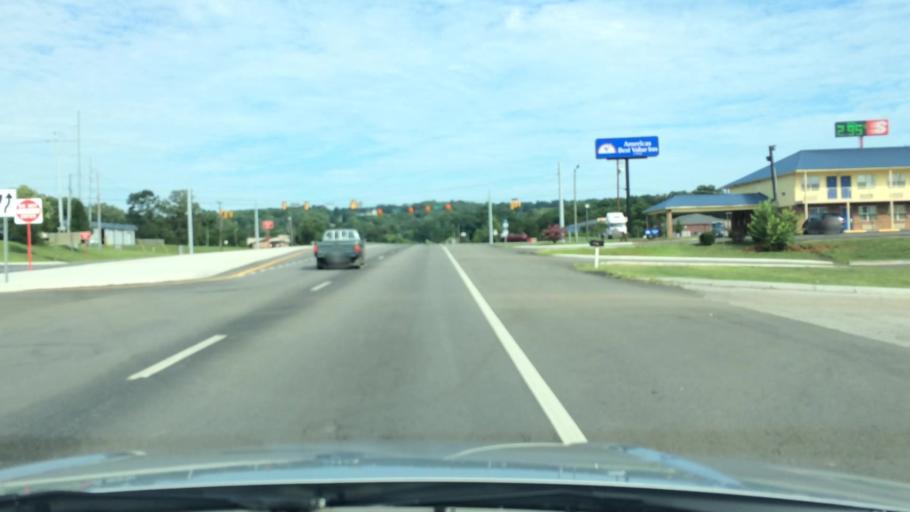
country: US
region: Tennessee
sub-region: McMinn County
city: Athens
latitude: 35.4674
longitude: -84.6511
